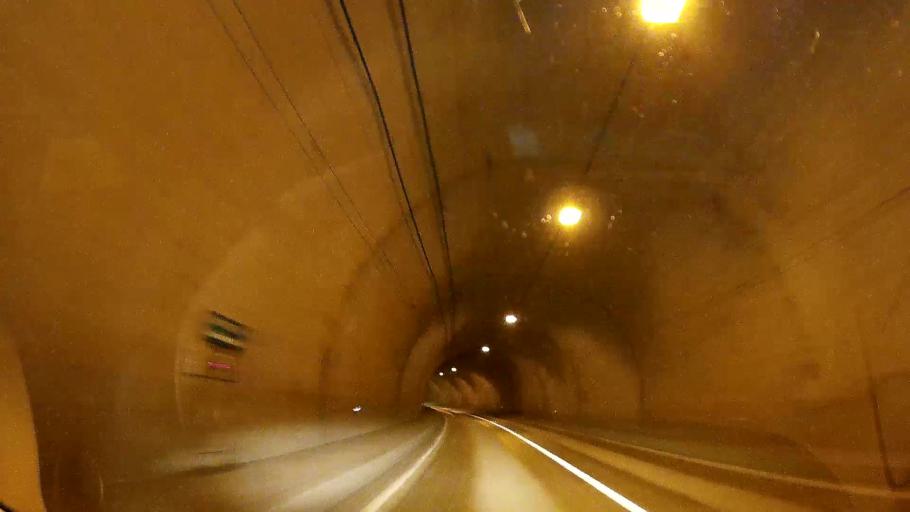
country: JP
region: Nagano
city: Toyoshina
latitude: 36.1928
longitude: 137.6239
